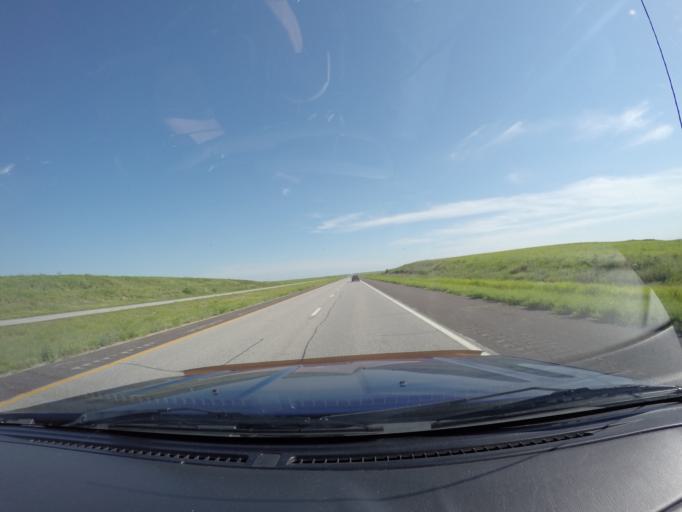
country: US
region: Kansas
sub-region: Riley County
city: Manhattan
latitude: 39.1254
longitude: -96.5384
